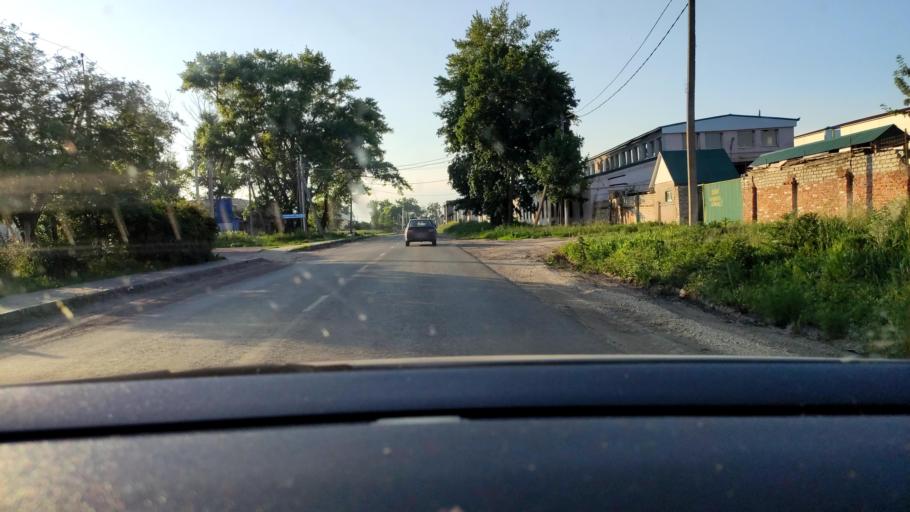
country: RU
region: Voronezj
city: Maslovka
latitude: 51.5390
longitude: 39.3416
